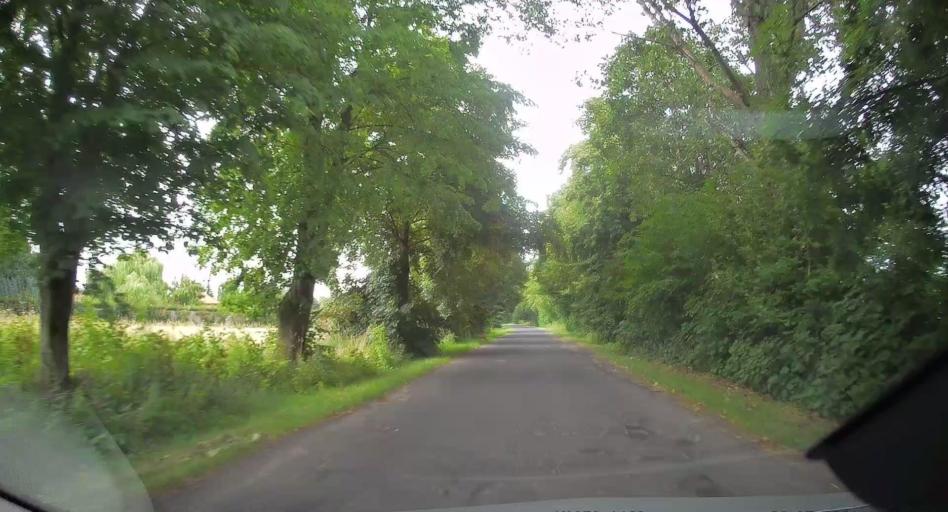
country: PL
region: Lodz Voivodeship
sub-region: Powiat rawski
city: Rawa Mazowiecka
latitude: 51.7679
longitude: 20.1835
